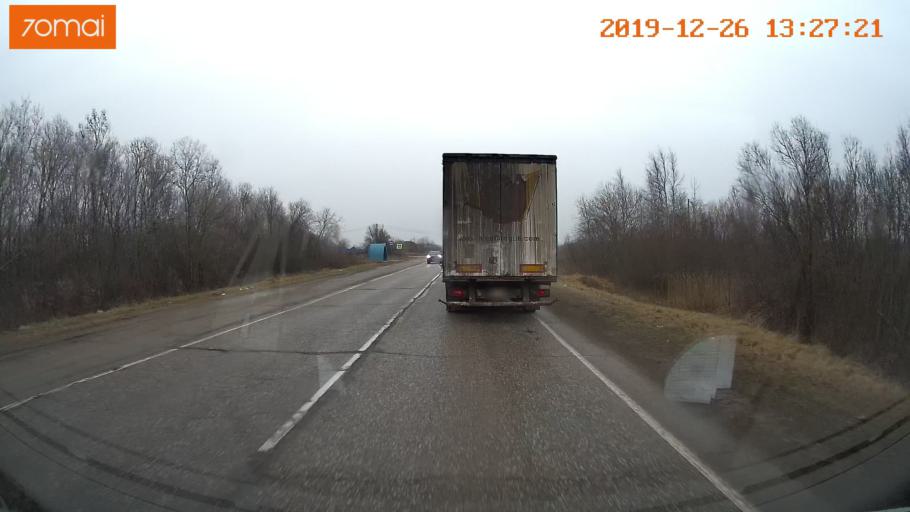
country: RU
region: Vologda
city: Cherepovets
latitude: 58.8543
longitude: 38.2390
